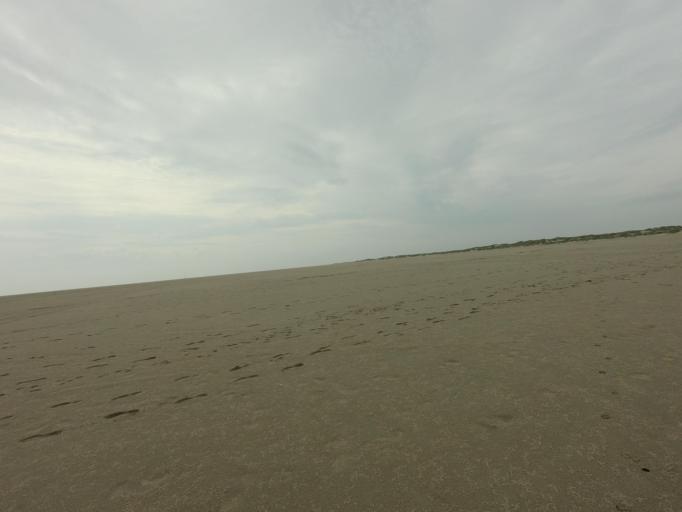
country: NL
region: North Holland
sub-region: Gemeente Den Helder
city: Den Helder
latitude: 52.9925
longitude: 4.7419
